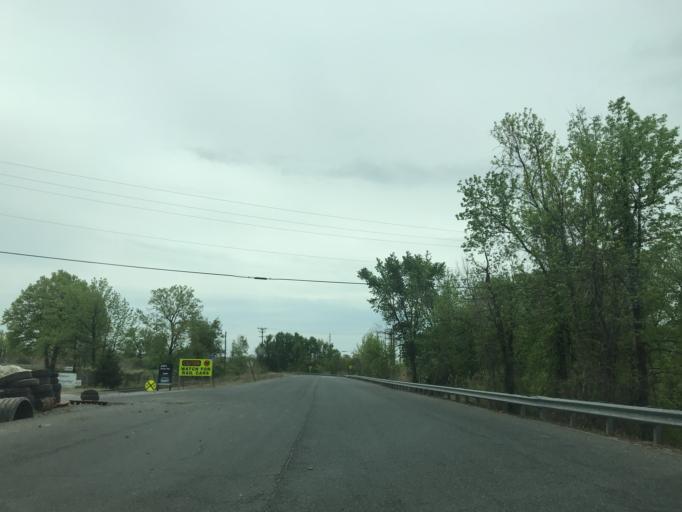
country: US
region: Maryland
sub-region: Baltimore County
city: Edgemere
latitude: 39.2469
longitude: -76.4680
